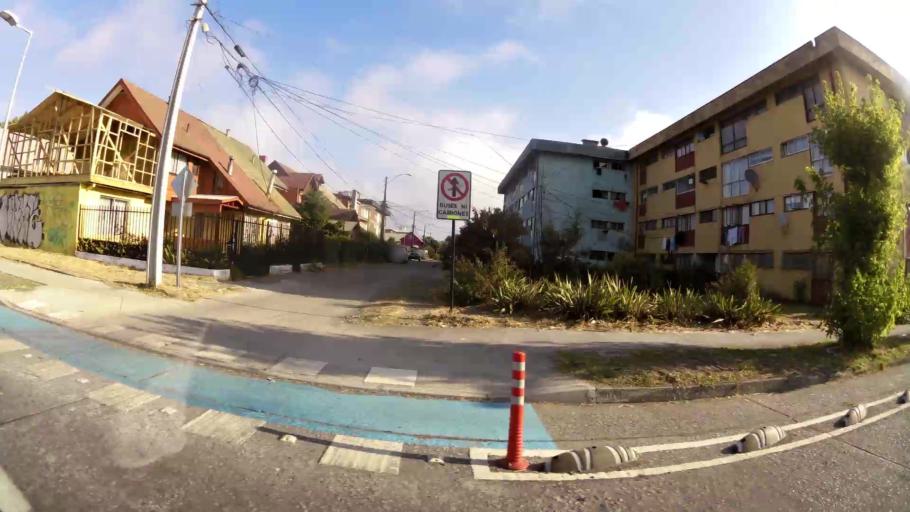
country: CL
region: Biobio
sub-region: Provincia de Concepcion
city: Concepcion
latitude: -36.7902
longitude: -73.0874
